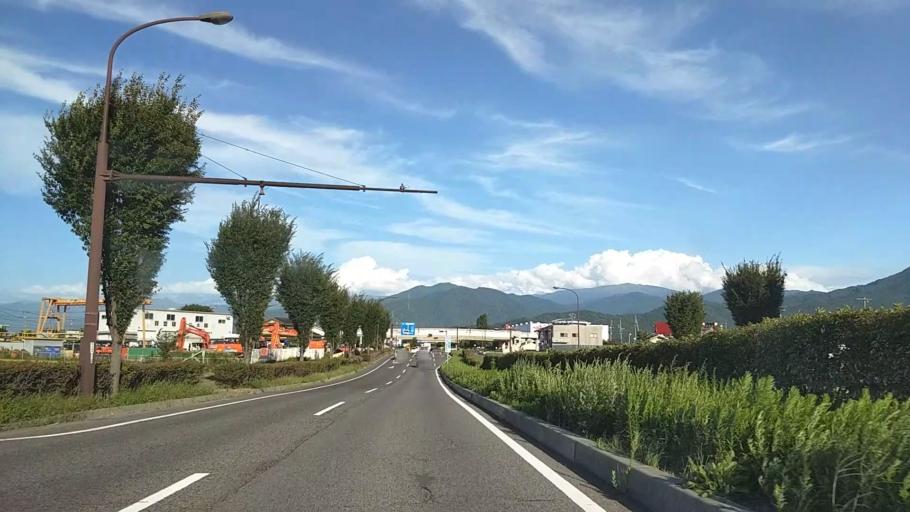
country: JP
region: Nagano
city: Nagano-shi
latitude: 36.6055
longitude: 138.1919
